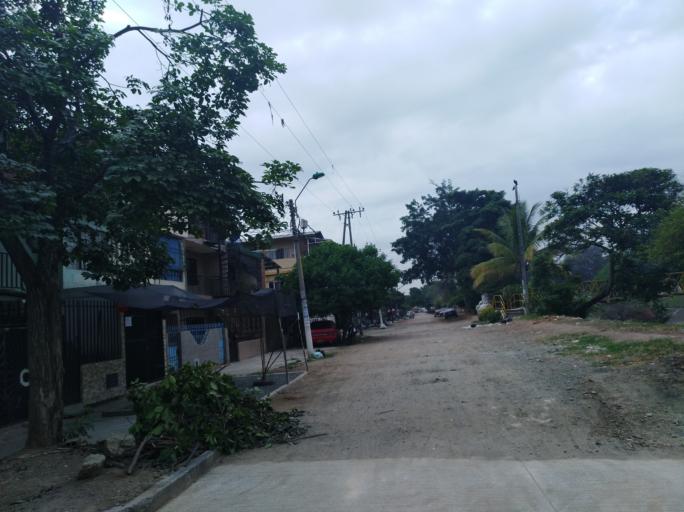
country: CO
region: Valle del Cauca
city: Cali
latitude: 3.4769
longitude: -76.4827
